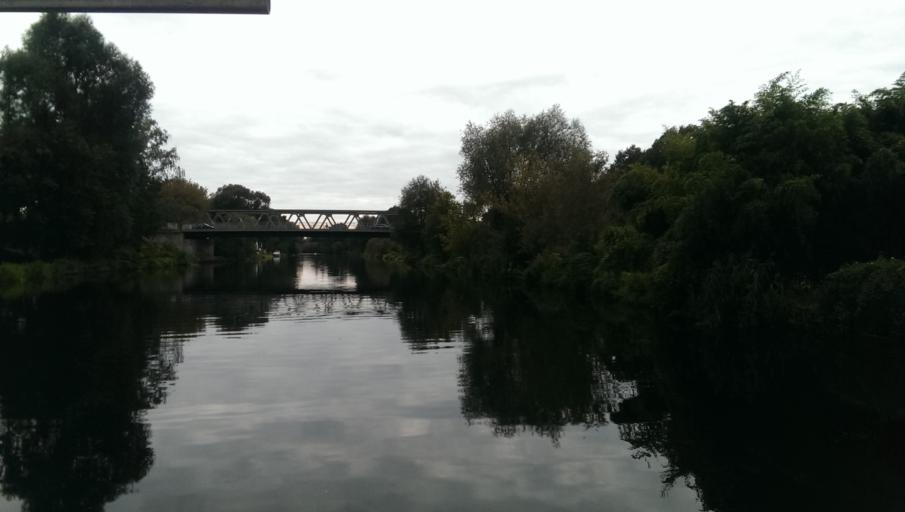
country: DE
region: Brandenburg
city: Oranienburg
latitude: 52.7442
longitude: 13.2588
